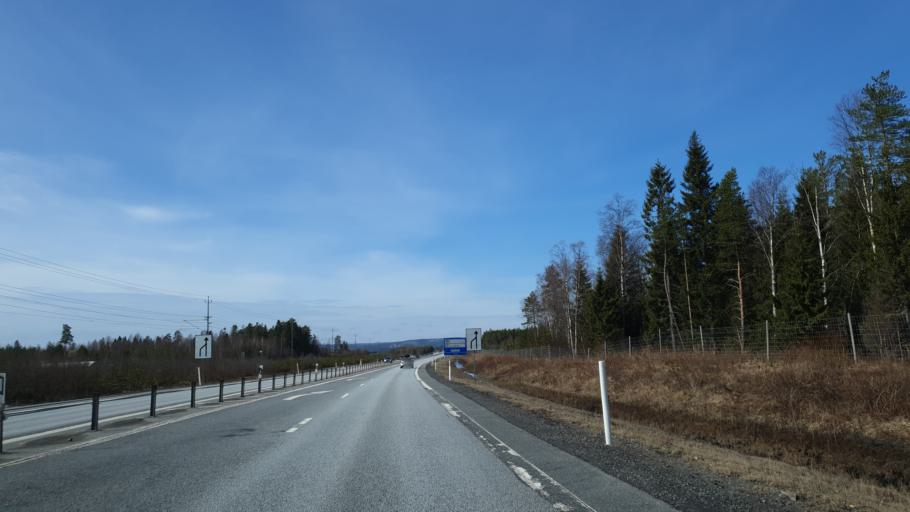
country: SE
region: Vaesterbotten
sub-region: Nordmalings Kommun
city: Nordmaling
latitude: 63.5806
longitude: 19.5086
